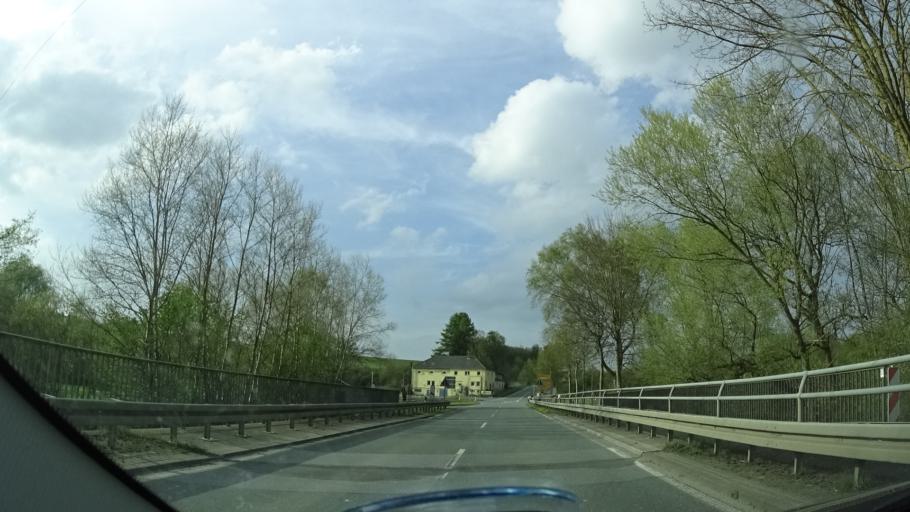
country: DE
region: North Rhine-Westphalia
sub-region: Regierungsbezirk Arnsberg
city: Ruthen
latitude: 51.4803
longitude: 8.4141
